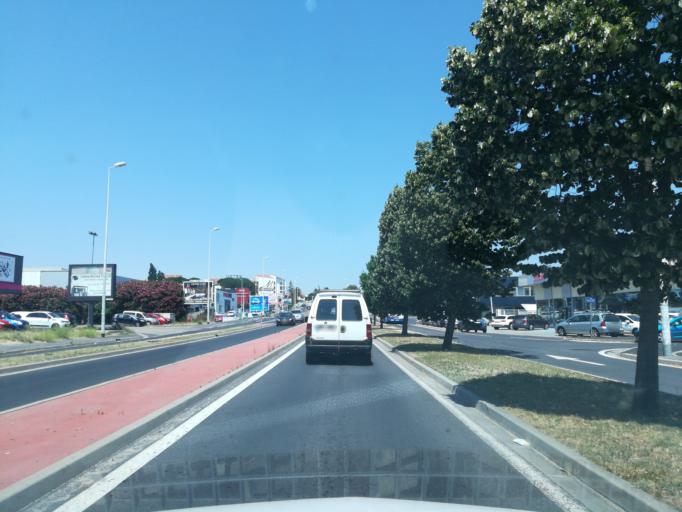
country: FR
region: Languedoc-Roussillon
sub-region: Departement des Pyrenees-Orientales
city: Perpignan
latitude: 42.6791
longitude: 2.8922
